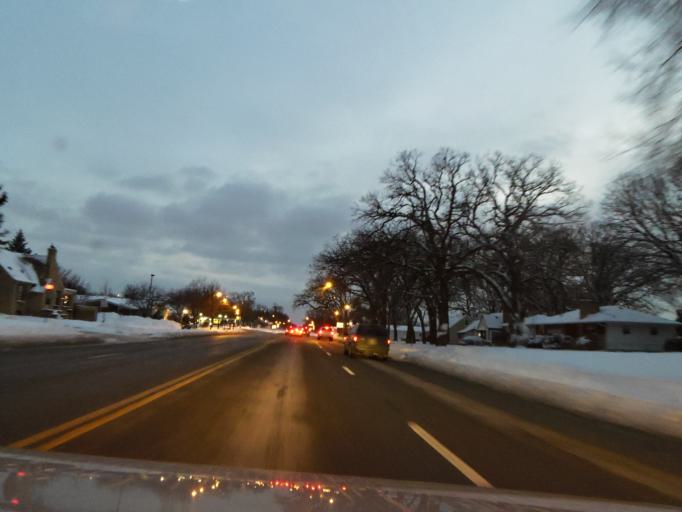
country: US
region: Minnesota
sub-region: Hennepin County
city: Richfield
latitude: 44.8853
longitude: -93.2679
